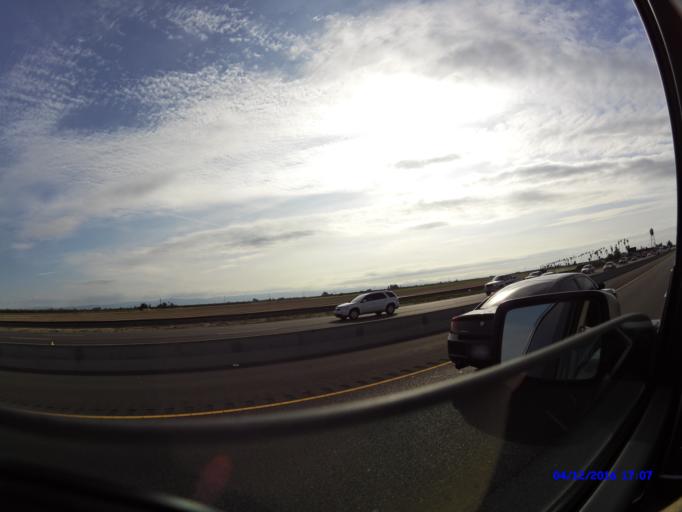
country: US
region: California
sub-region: San Joaquin County
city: Ripon
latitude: 37.7617
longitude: -121.1586
